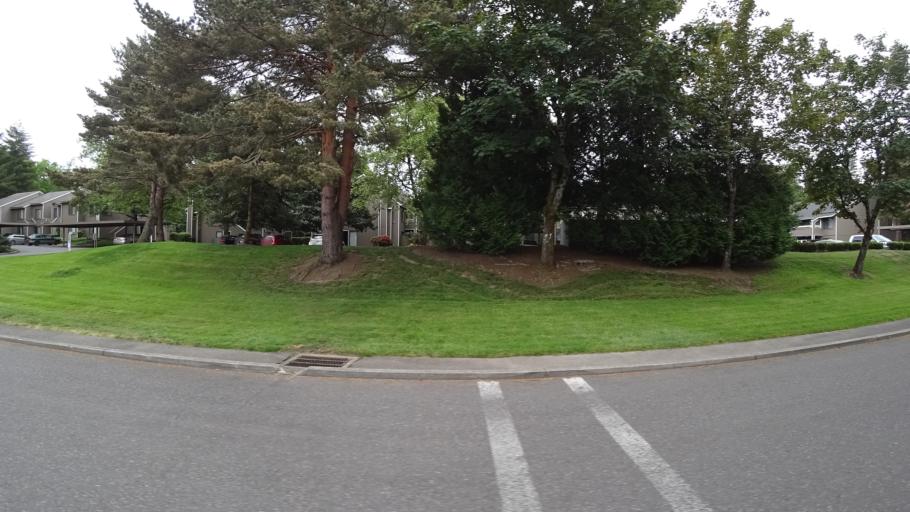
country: US
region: Oregon
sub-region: Washington County
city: Raleigh Hills
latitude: 45.4765
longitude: -122.7499
